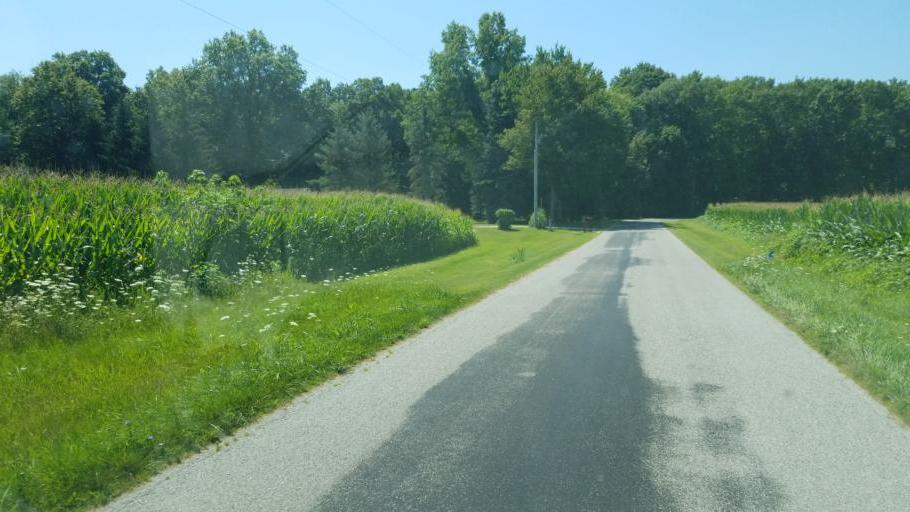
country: US
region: Ohio
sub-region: Delaware County
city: Ashley
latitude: 40.4696
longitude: -83.0570
